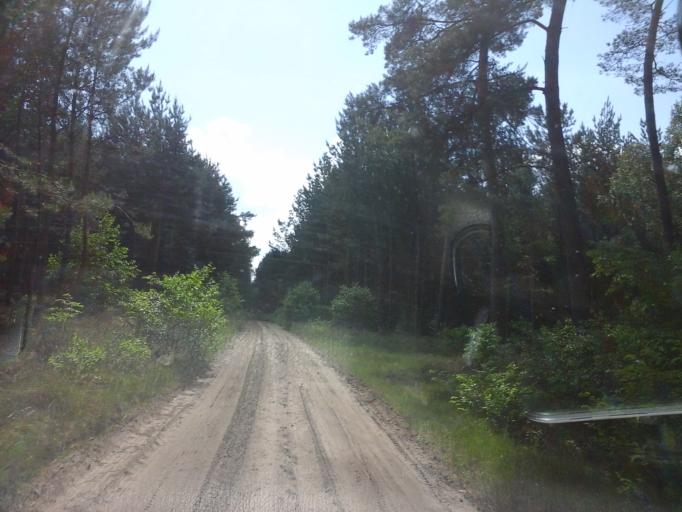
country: PL
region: West Pomeranian Voivodeship
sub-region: Powiat choszczenski
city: Bierzwnik
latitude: 53.1272
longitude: 15.6671
